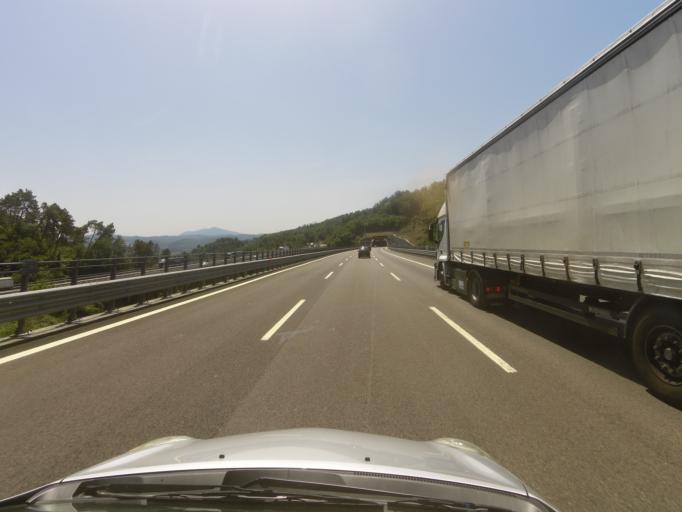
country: IT
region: Tuscany
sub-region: Province of Florence
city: Barberino di Mugello
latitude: 44.0123
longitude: 11.2196
